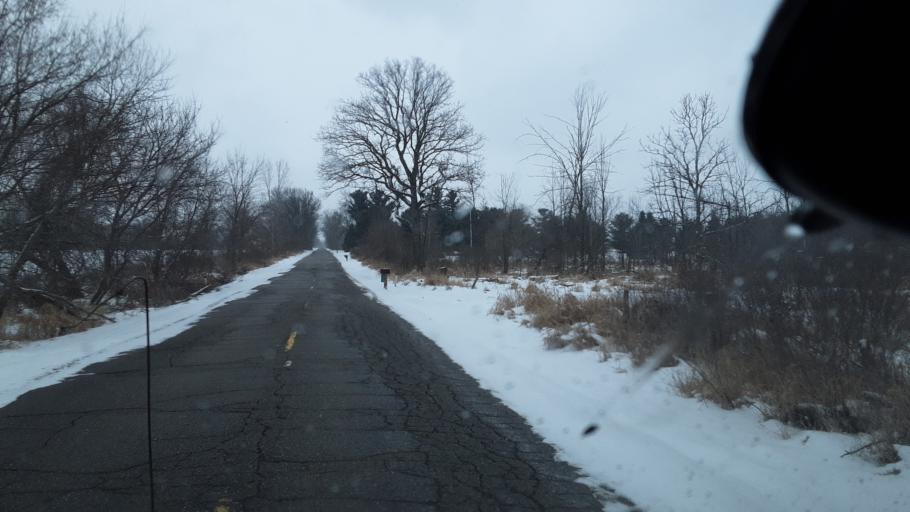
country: US
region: Michigan
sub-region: Ingham County
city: Leslie
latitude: 42.4780
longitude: -84.3941
